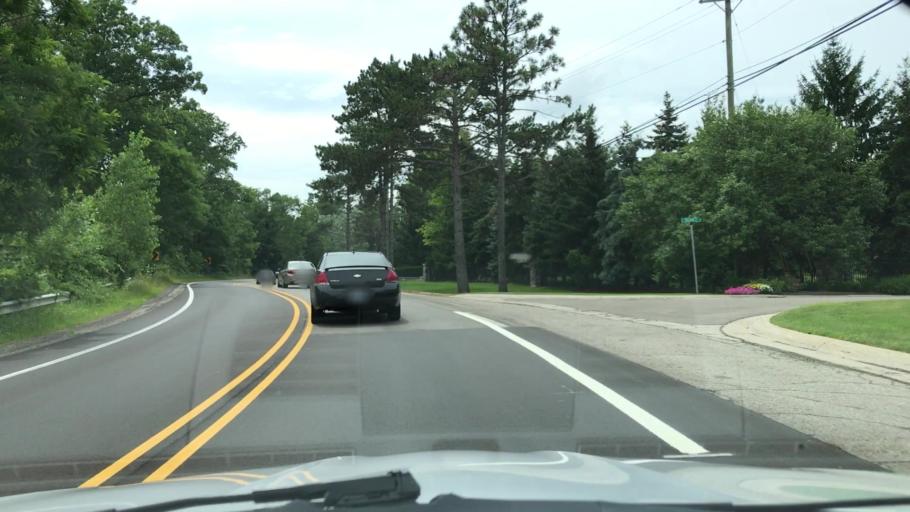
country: US
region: Michigan
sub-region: Oakland County
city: West Bloomfield Township
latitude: 42.5718
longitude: -83.3871
